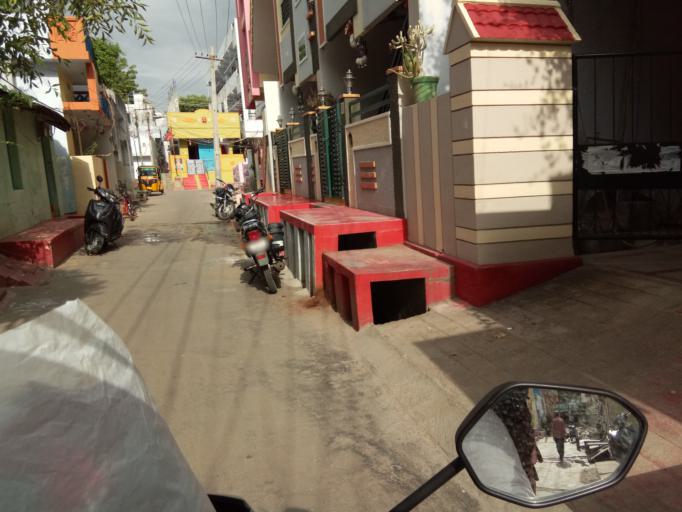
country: IN
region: Telangana
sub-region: Khammam
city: Khammam
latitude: 17.2420
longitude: 80.1424
